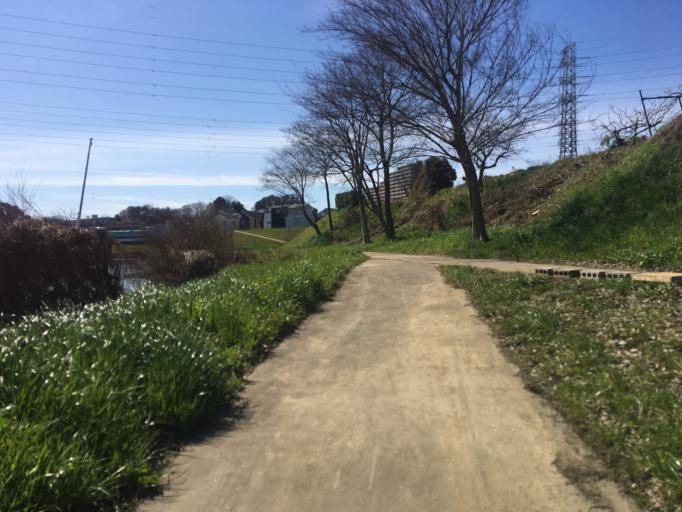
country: JP
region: Saitama
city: Asaka
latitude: 35.8127
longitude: 139.6093
